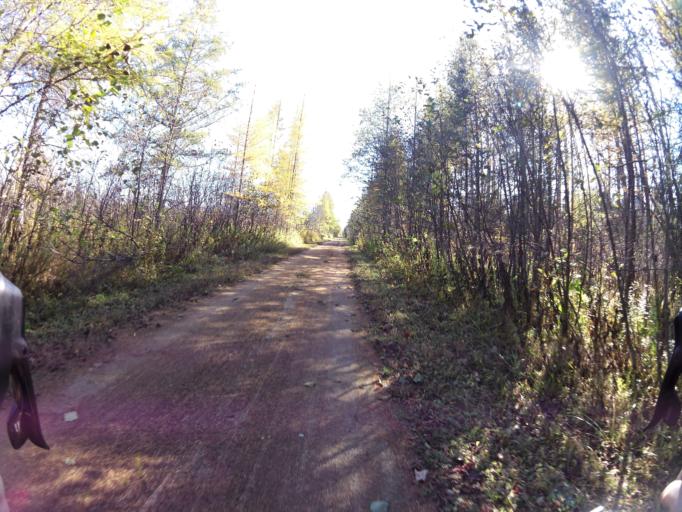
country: CA
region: Quebec
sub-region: Outaouais
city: Wakefield
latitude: 45.8953
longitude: -76.0358
